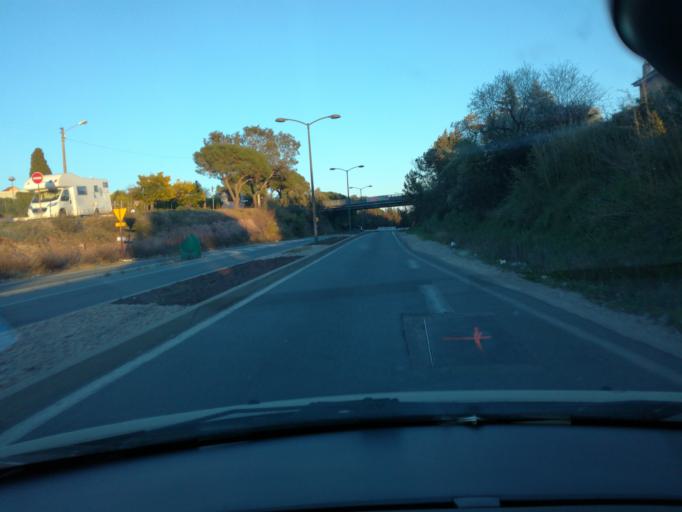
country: FR
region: Provence-Alpes-Cote d'Azur
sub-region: Departement du Var
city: Puget-sur-Argens
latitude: 43.4571
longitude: 6.6851
